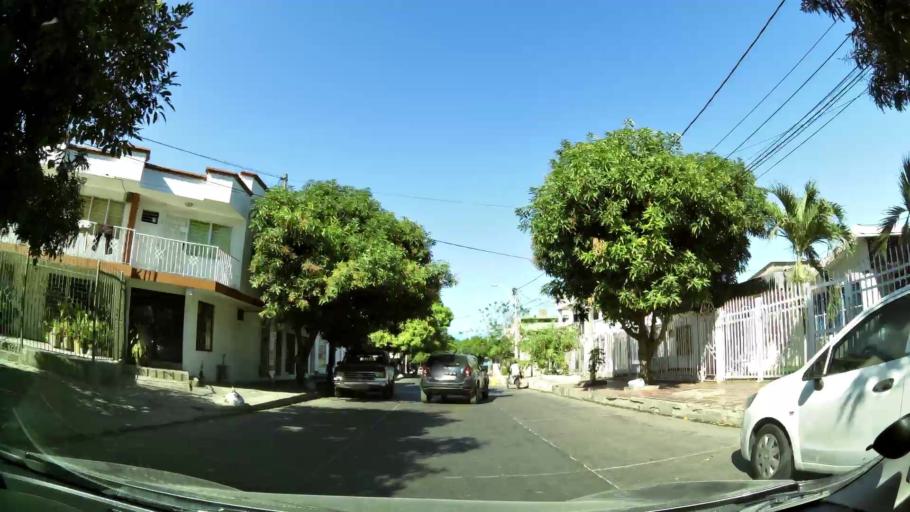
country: CO
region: Atlantico
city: Barranquilla
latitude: 10.9500
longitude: -74.7918
